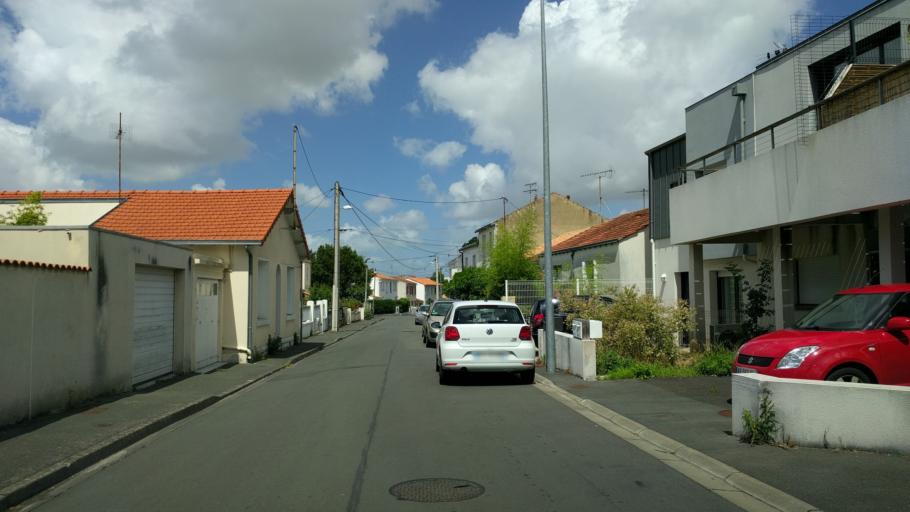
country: FR
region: Poitou-Charentes
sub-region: Departement de la Charente-Maritime
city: La Rochelle
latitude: 46.1736
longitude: -1.1407
